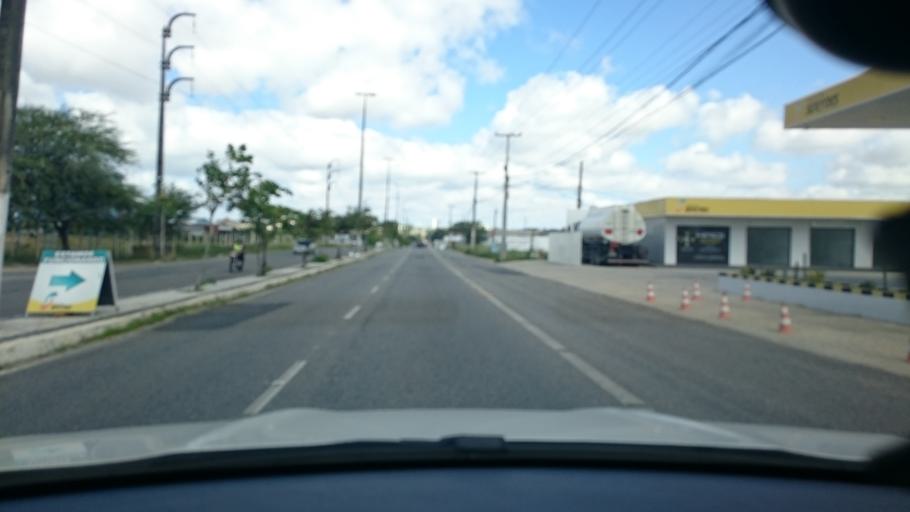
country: BR
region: Paraiba
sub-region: Campina Grande
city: Campina Grande
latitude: -7.2332
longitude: -35.9141
